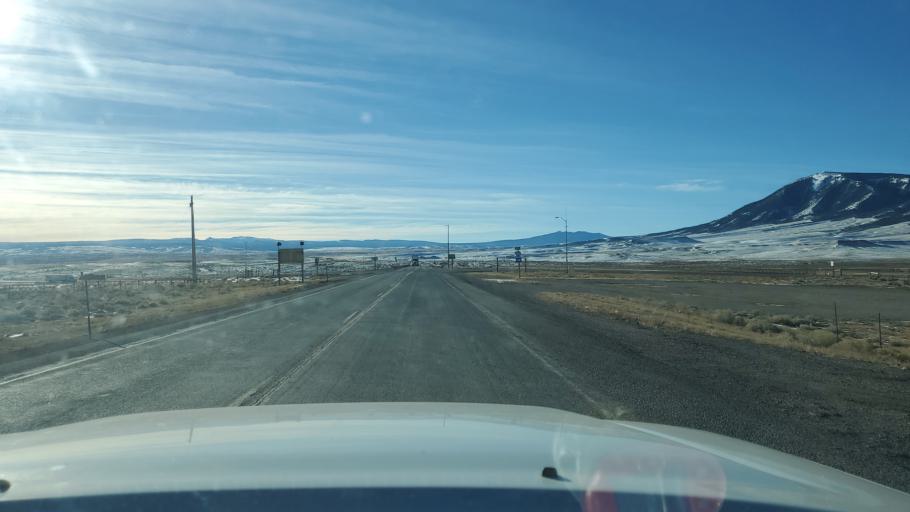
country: US
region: Wyoming
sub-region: Carbon County
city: Saratoga
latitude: 41.7269
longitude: -106.4600
